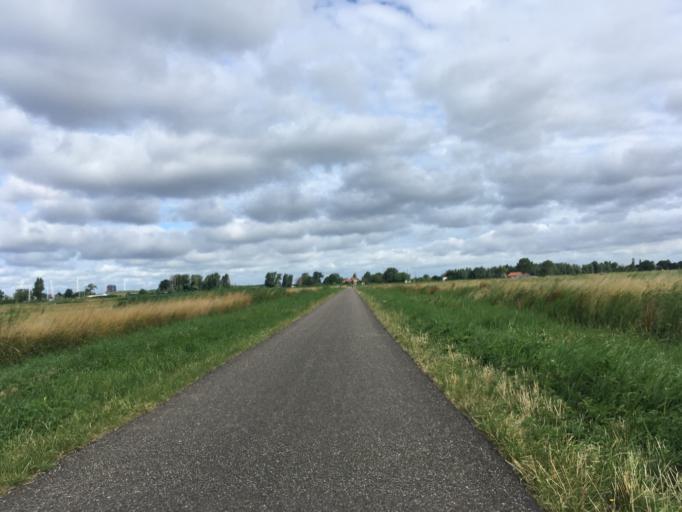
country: NL
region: North Holland
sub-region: Gemeente Haarlem
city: Haarlem
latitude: 52.3982
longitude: 4.6860
